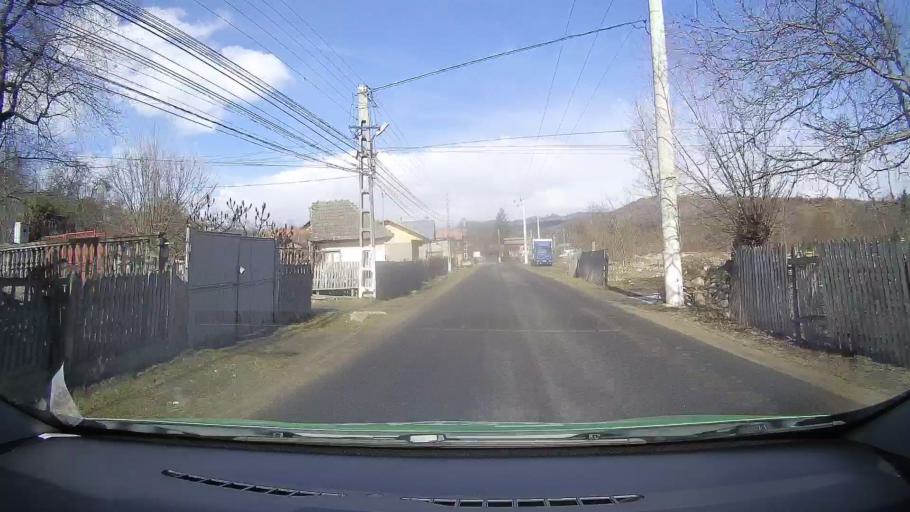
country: RO
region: Dambovita
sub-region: Comuna Runcu
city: Badeni
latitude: 45.1690
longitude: 25.3947
